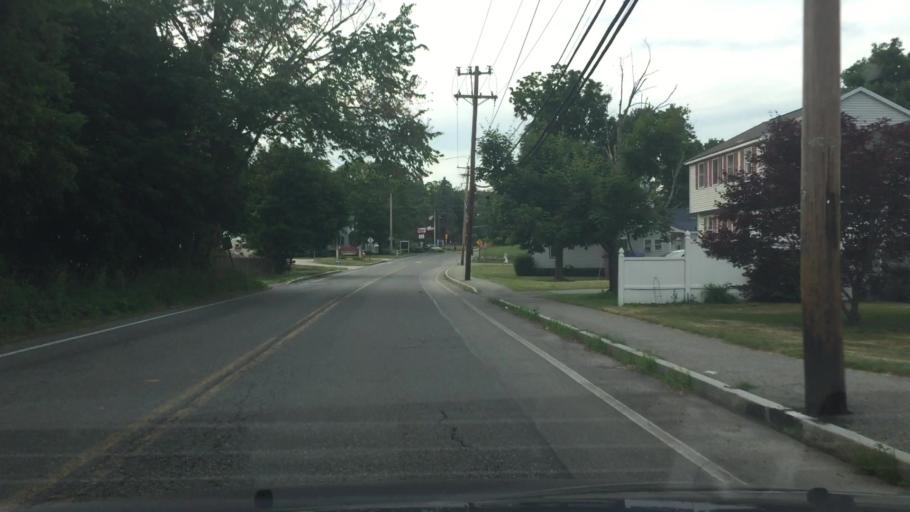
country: US
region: Massachusetts
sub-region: Middlesex County
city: Dracut
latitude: 42.6807
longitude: -71.3536
